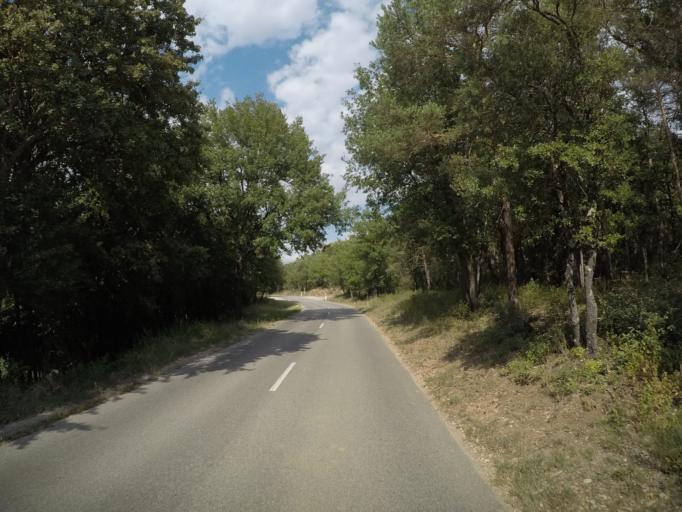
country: FR
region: Provence-Alpes-Cote d'Azur
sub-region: Departement des Alpes-de-Haute-Provence
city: Valensole
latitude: 43.8062
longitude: 5.9537
